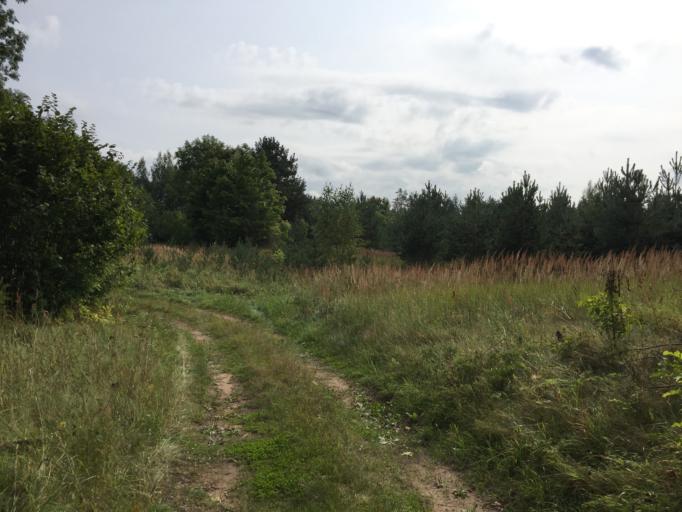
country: LV
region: Cibla
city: Cibla
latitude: 56.2413
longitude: 27.8298
